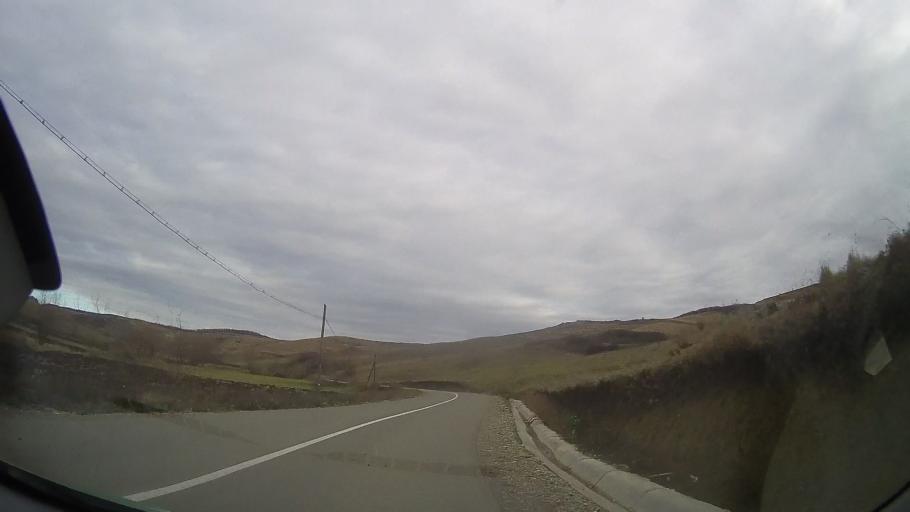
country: RO
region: Bistrita-Nasaud
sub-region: Comuna Silvasu de Campie
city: Silvasu de Campie
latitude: 46.8216
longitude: 24.3001
